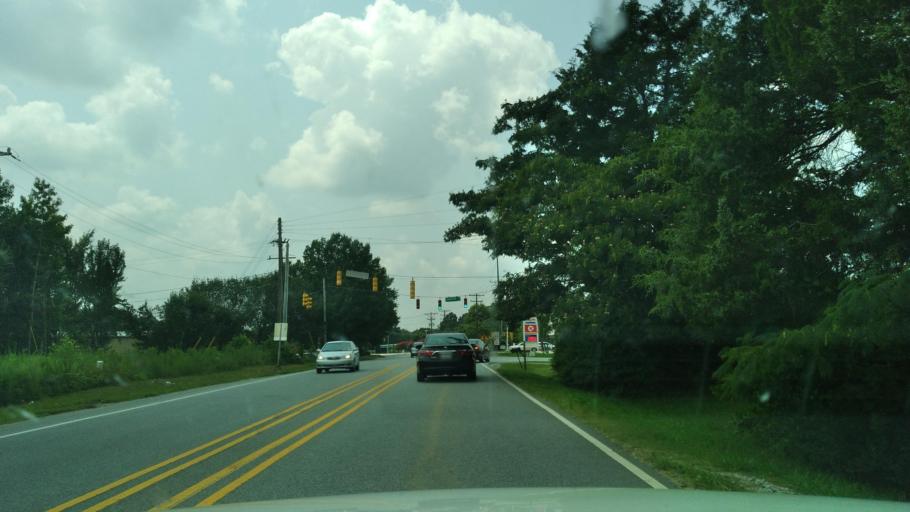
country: US
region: North Carolina
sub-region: Guilford County
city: Summerfield
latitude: 36.1254
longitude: -79.9035
